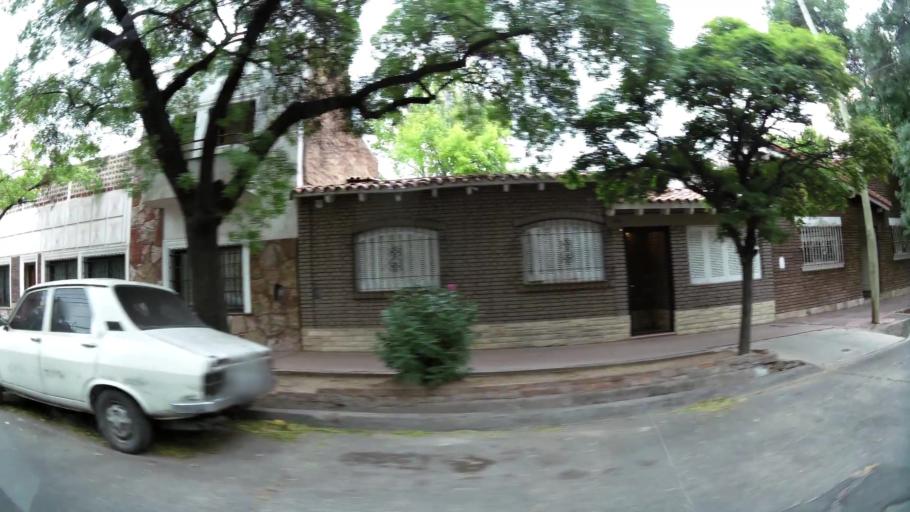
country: AR
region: Mendoza
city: Mendoza
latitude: -32.8766
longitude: -68.8546
